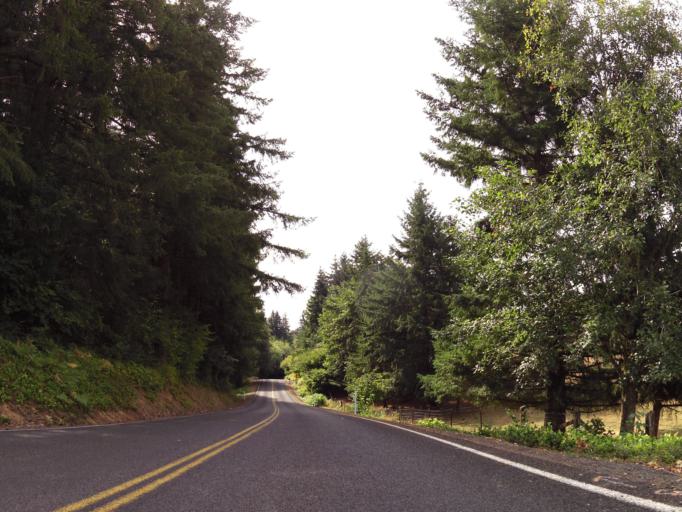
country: US
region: Washington
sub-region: Lewis County
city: Chehalis
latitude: 46.5973
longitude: -122.9712
